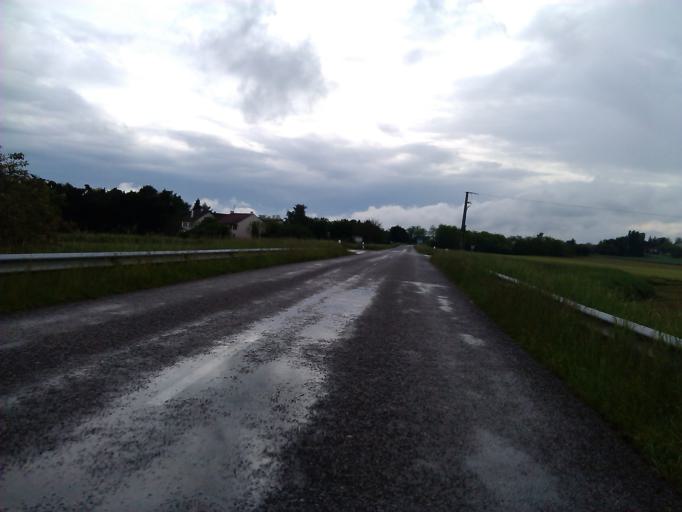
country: FR
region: Bourgogne
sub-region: Departement de Saone-et-Loire
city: Verdun-sur-le-Doubs
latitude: 46.9079
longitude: 4.9989
